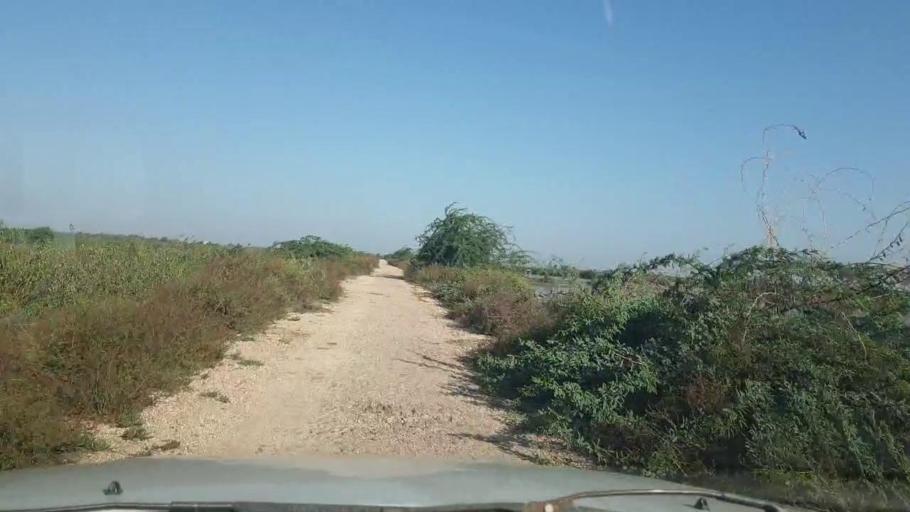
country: PK
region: Sindh
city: Chuhar Jamali
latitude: 24.5507
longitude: 67.9095
